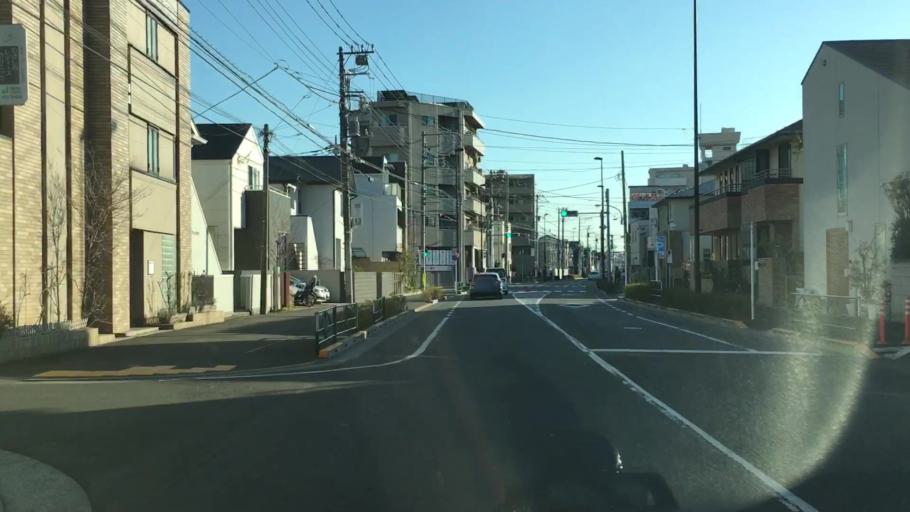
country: JP
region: Tokyo
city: Kamirenjaku
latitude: 35.7016
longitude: 139.5386
